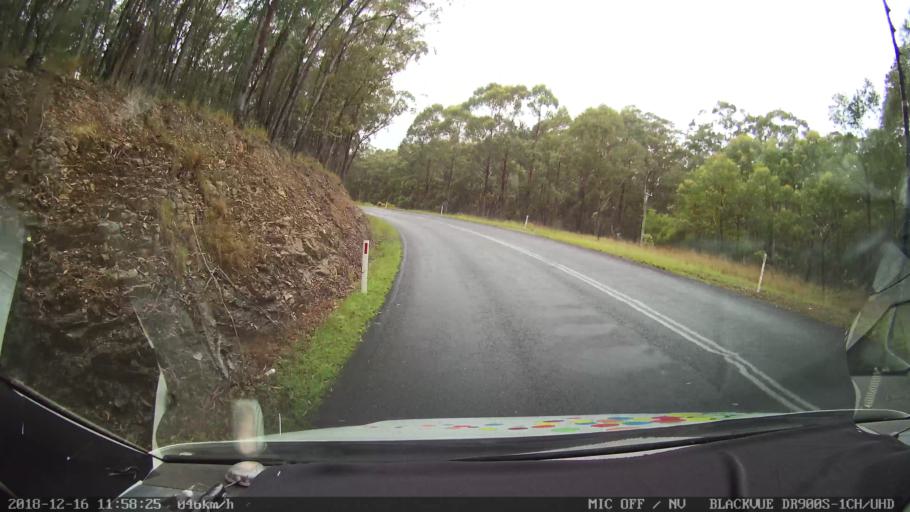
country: AU
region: New South Wales
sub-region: Tenterfield Municipality
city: Carrolls Creek
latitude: -28.9223
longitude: 152.3128
